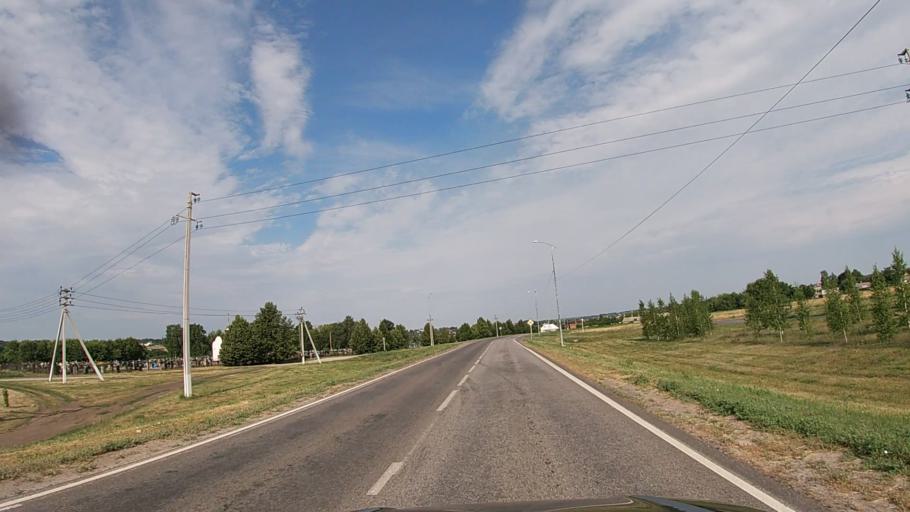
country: RU
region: Belgorod
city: Krasnaya Yaruga
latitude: 50.7984
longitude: 35.6810
